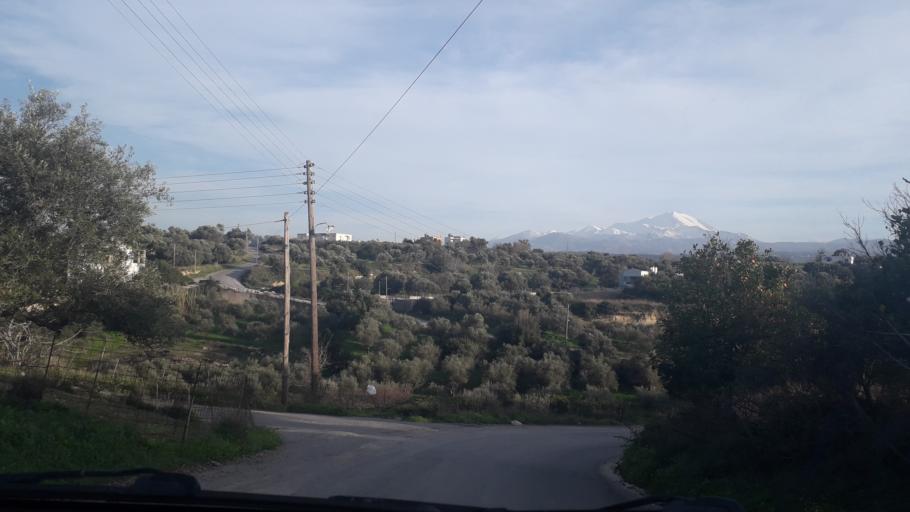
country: GR
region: Crete
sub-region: Nomos Rethymnis
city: Panormos
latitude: 35.3862
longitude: 24.6150
